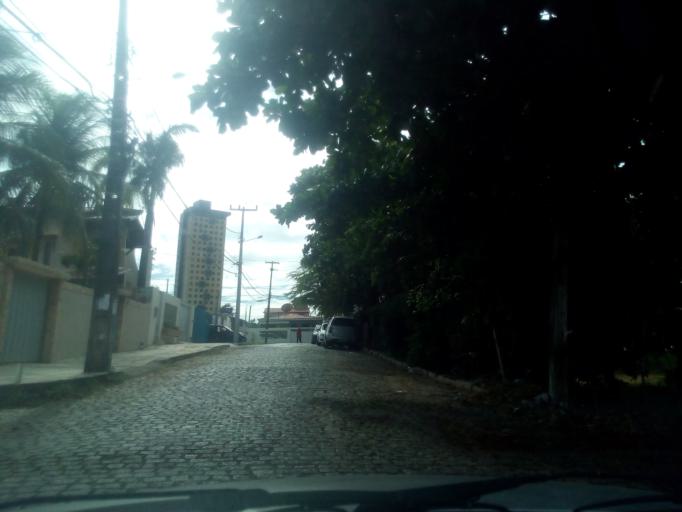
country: BR
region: Rio Grande do Norte
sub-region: Parnamirim
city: Parnamirim
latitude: -5.8703
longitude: -35.2091
